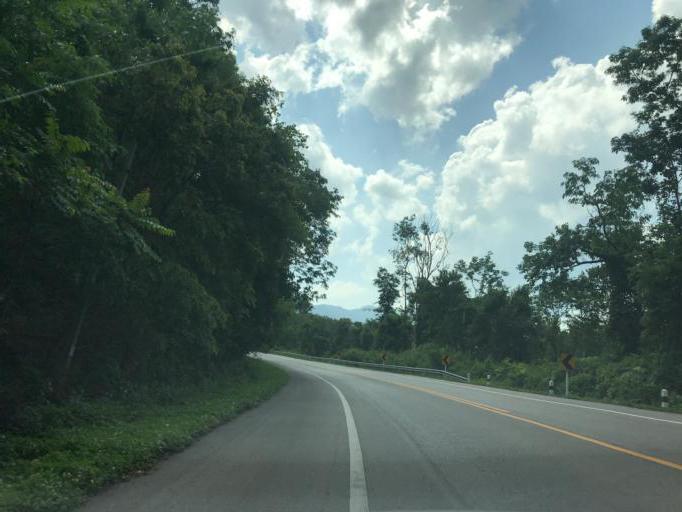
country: TH
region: Phayao
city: Phayao
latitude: 19.0891
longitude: 99.8130
